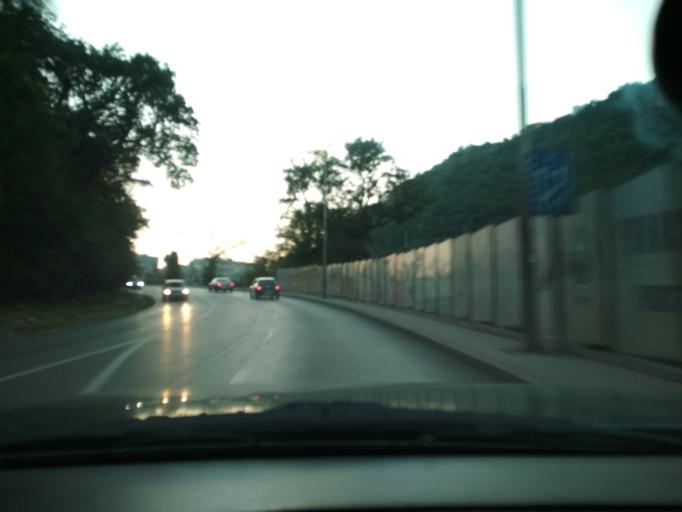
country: ME
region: Herceg Novi
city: Herceg-Novi
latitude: 42.4556
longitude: 18.5520
